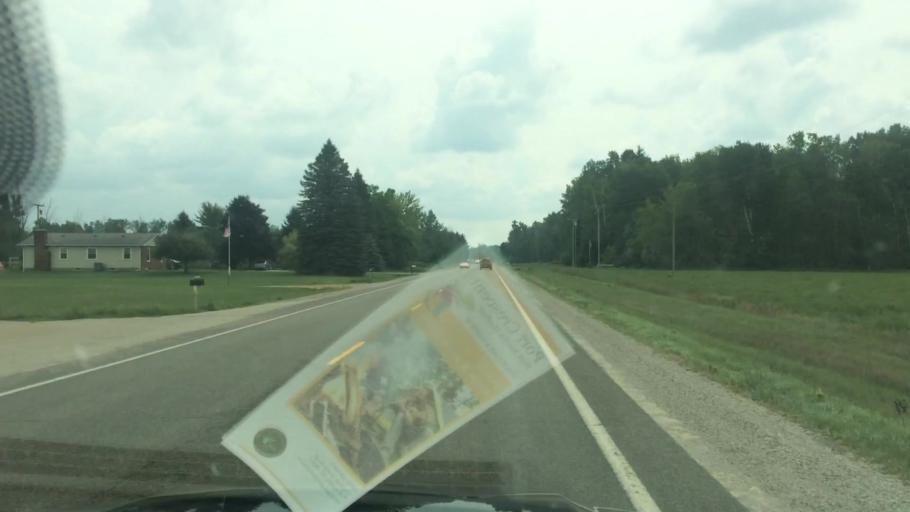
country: US
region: Michigan
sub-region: Tuscola County
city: Cass City
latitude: 43.6550
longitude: -83.0983
